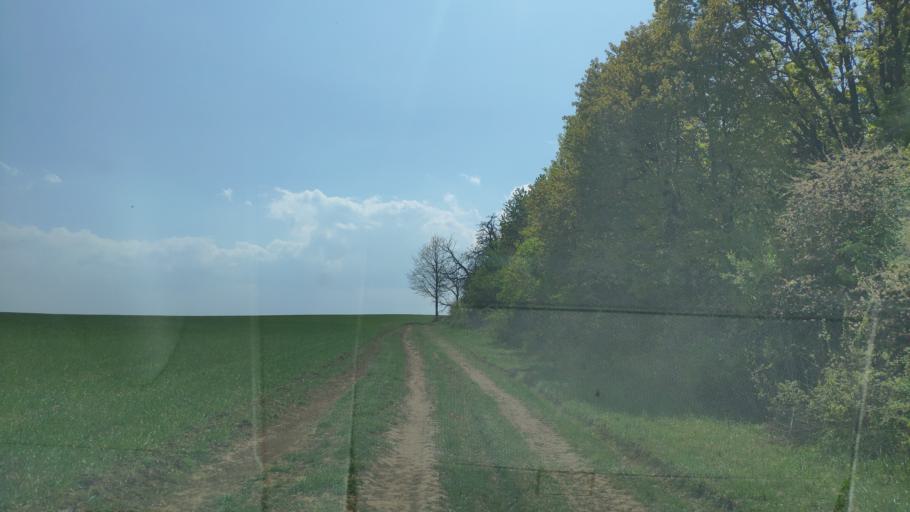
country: SK
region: Kosicky
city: Moldava nad Bodvou
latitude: 48.5480
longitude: 20.9475
